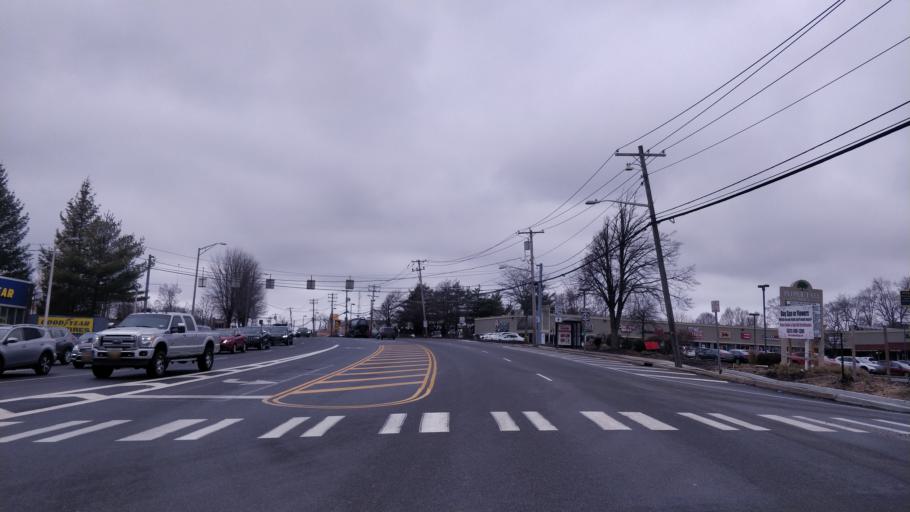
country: US
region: New York
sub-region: Suffolk County
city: Commack
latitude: 40.8431
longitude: -73.2931
